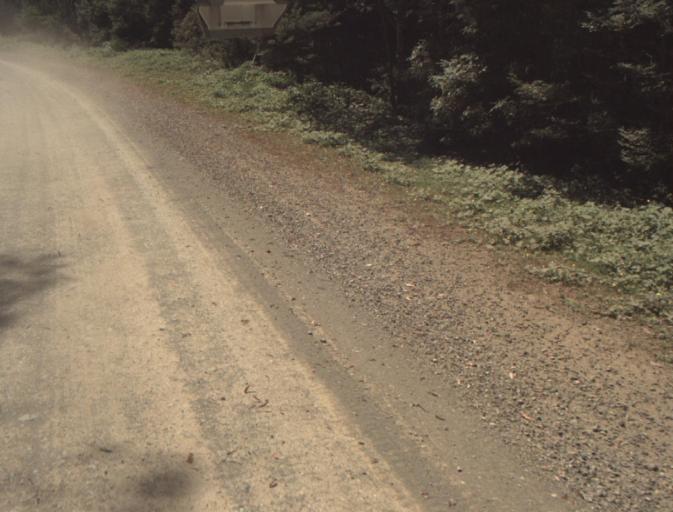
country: AU
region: Tasmania
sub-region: Dorset
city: Scottsdale
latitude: -41.3211
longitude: 147.4148
